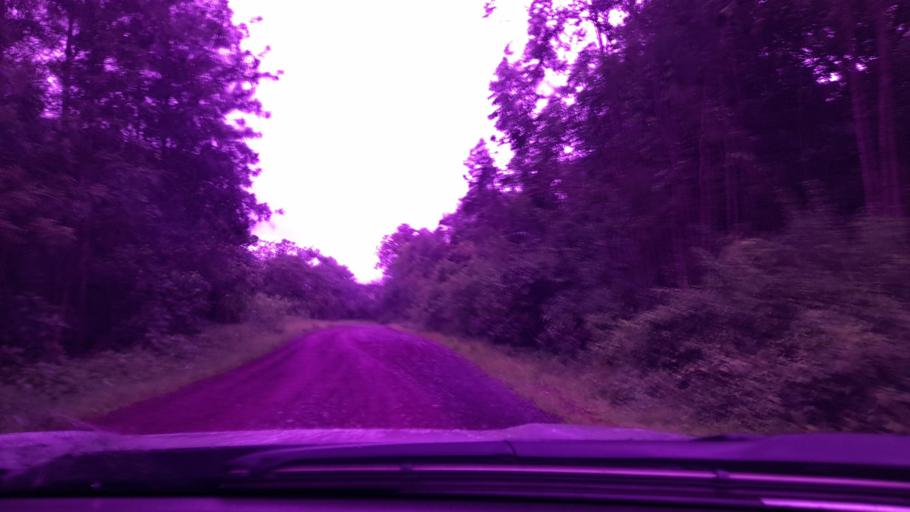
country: ET
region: Oromiya
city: Metu
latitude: 8.4481
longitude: 35.6289
